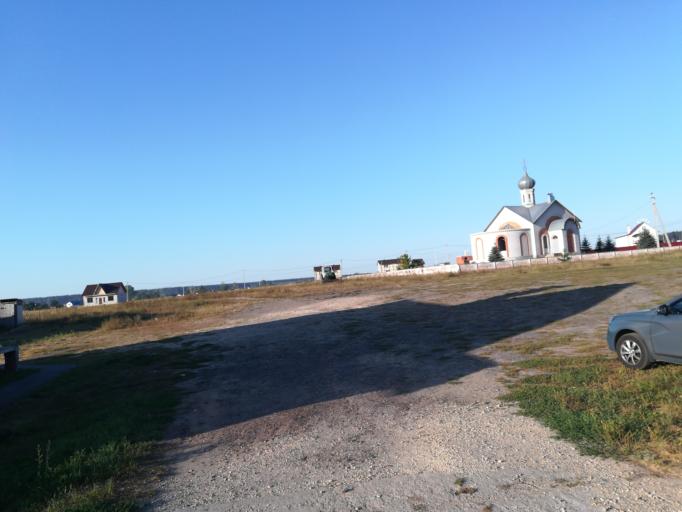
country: RU
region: Brjansk
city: Karachev
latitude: 53.1286
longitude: 34.9346
